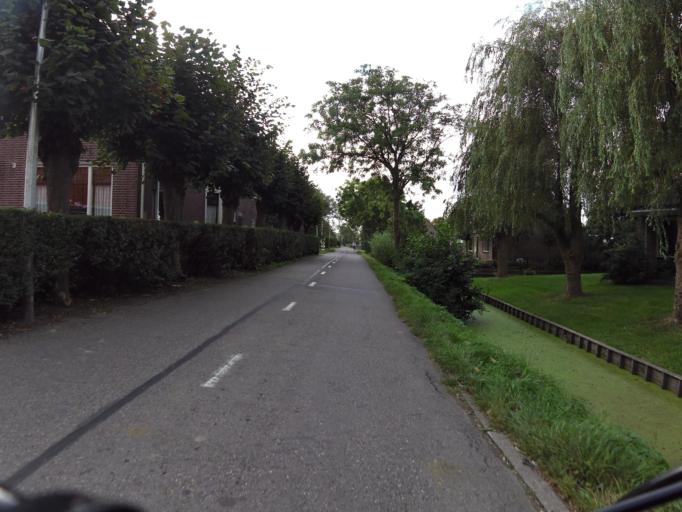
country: NL
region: South Holland
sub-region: Gemeente Leiderdorp
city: Leiderdorp
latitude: 52.1156
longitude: 4.5242
